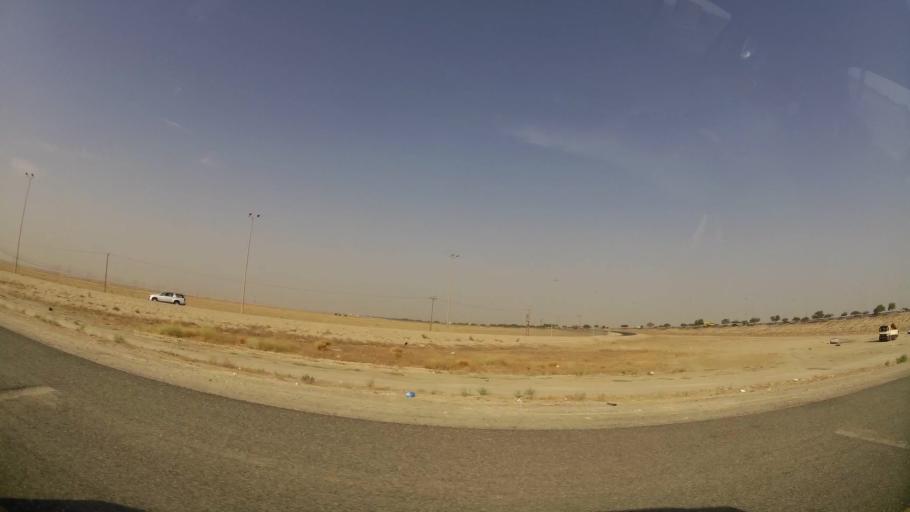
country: KW
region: Al Farwaniyah
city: Janub as Surrah
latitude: 29.1774
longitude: 47.9900
